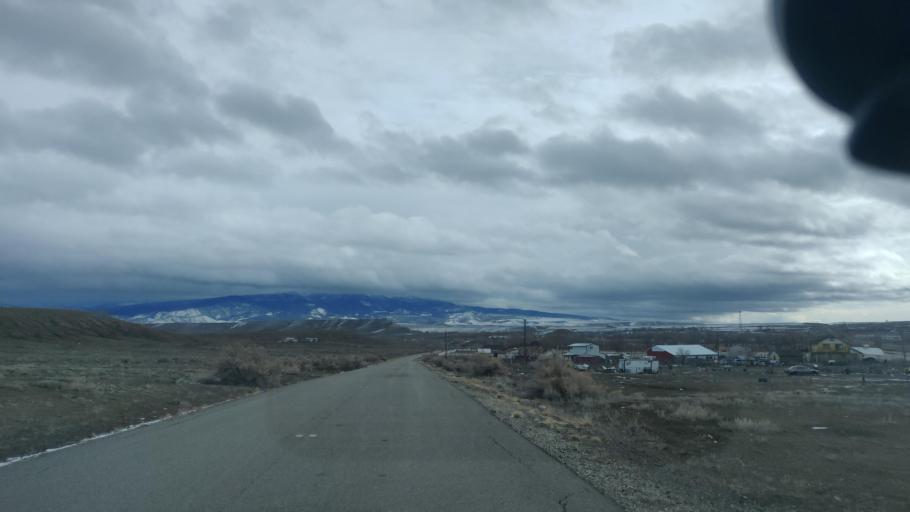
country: US
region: Colorado
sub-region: Mesa County
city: Clifton
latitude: 38.9440
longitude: -108.4053
